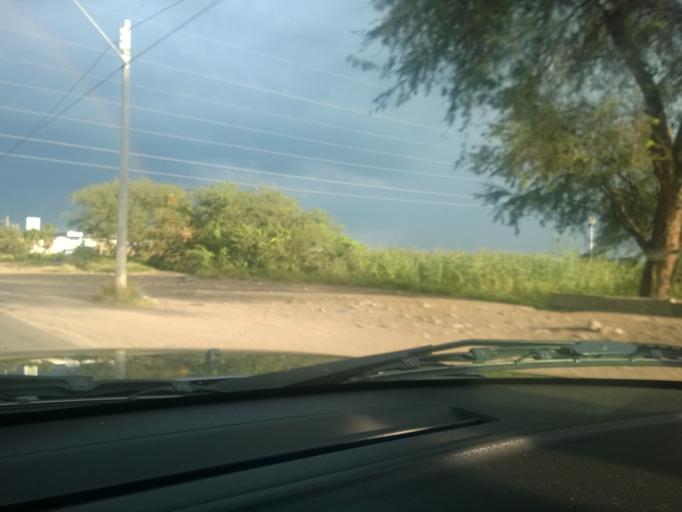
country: MX
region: Guanajuato
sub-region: Leon
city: Fraccionamiento Paraiso Real
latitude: 21.1107
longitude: -101.5997
